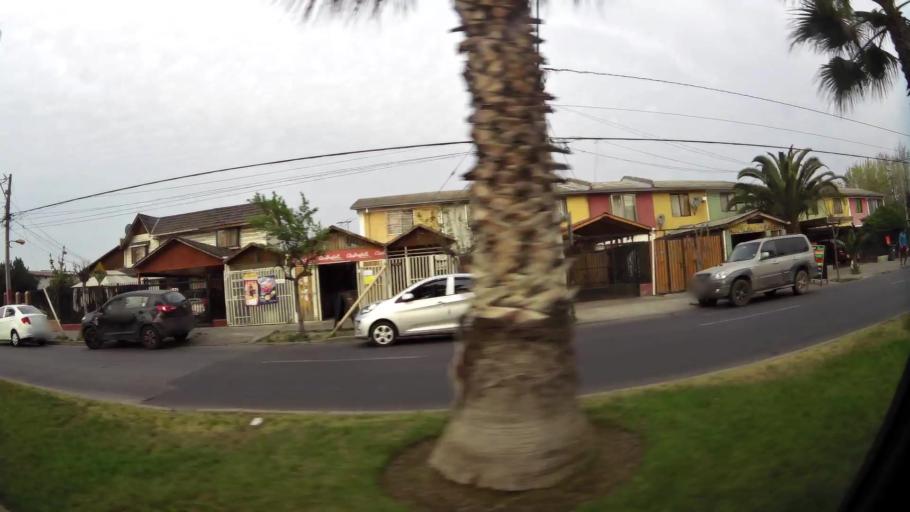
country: CL
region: Santiago Metropolitan
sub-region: Provincia de Santiago
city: Lo Prado
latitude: -33.5230
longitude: -70.7968
